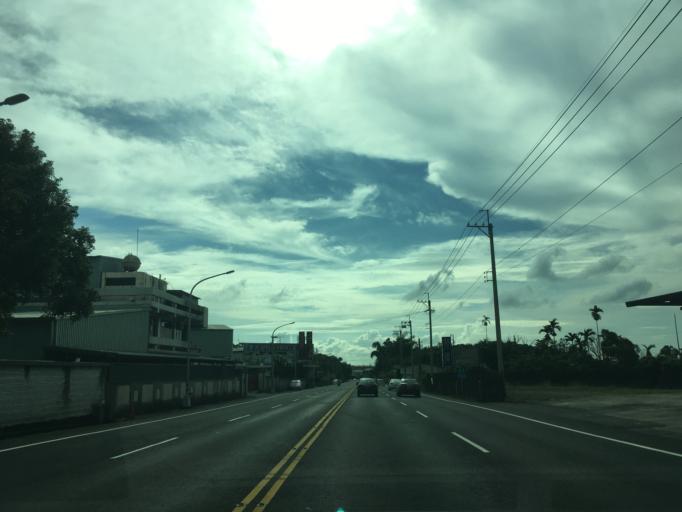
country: TW
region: Taiwan
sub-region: Chiayi
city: Jiayi Shi
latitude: 23.4443
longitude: 120.5053
